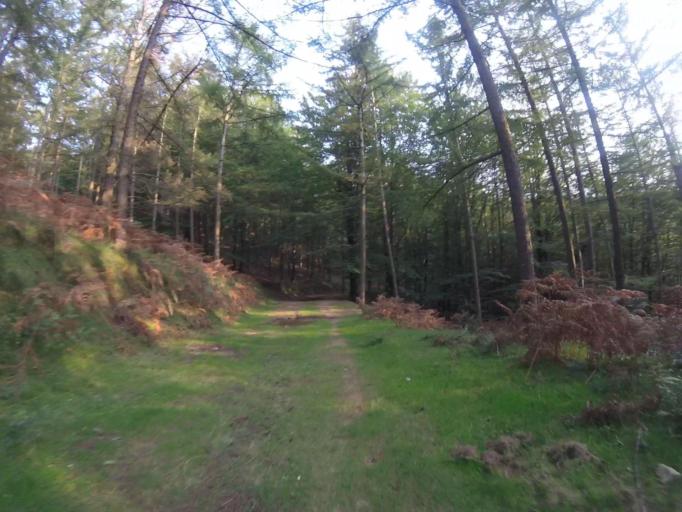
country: ES
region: Navarre
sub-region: Provincia de Navarra
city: Arano
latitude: 43.2591
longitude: -1.8339
